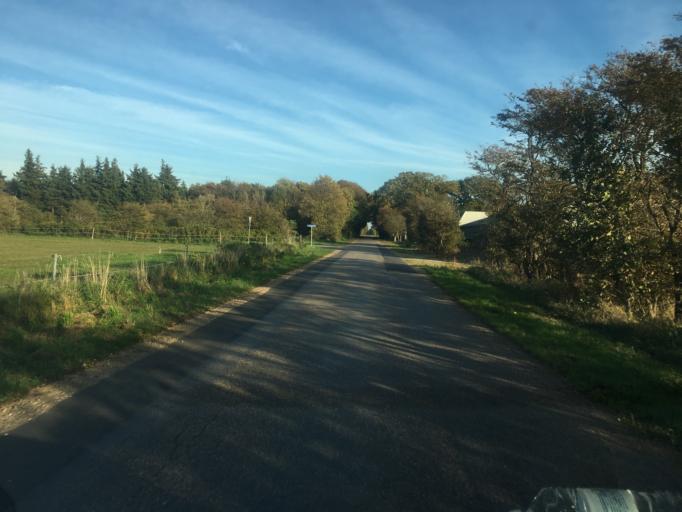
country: DE
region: Schleswig-Holstein
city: Ellhoft
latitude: 54.9162
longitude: 8.9650
